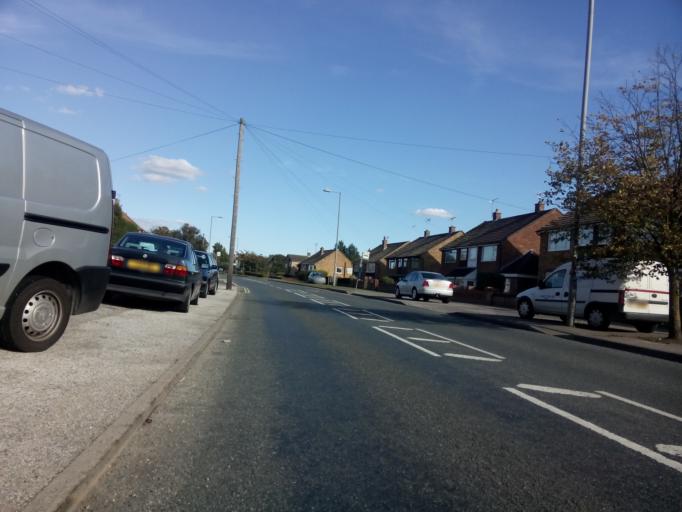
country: GB
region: England
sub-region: Suffolk
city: Bramford
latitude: 52.0441
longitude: 1.1167
